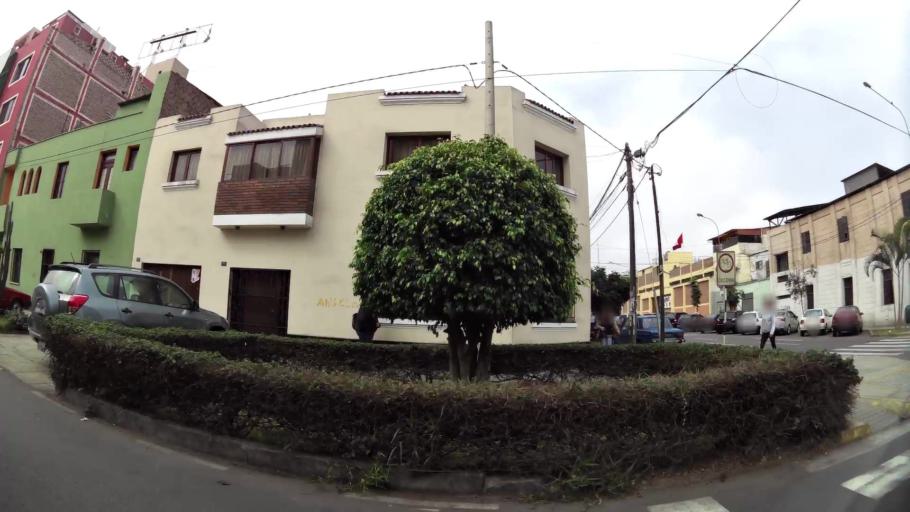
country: PE
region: Lima
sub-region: Lima
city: San Isidro
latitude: -12.0819
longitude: -77.0393
